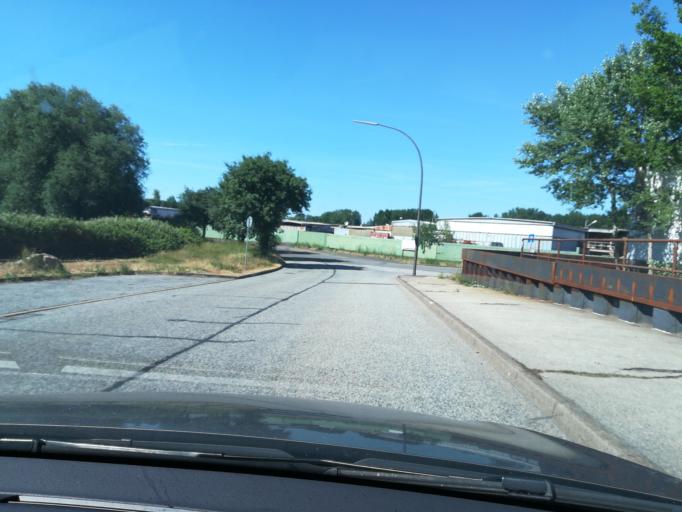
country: DE
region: Hamburg
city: Rothenburgsort
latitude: 53.5230
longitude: 10.0433
